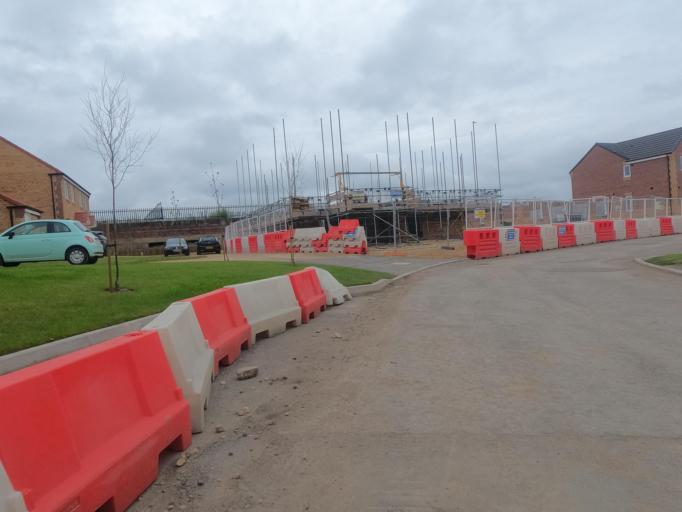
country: GB
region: England
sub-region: Northumberland
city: Blyth
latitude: 55.1324
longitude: -1.5284
